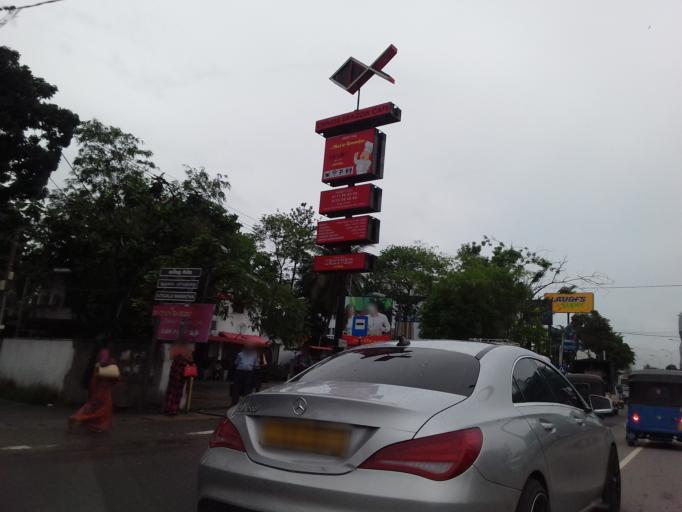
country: LK
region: Western
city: Pita Kotte
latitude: 6.9077
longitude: 79.8997
